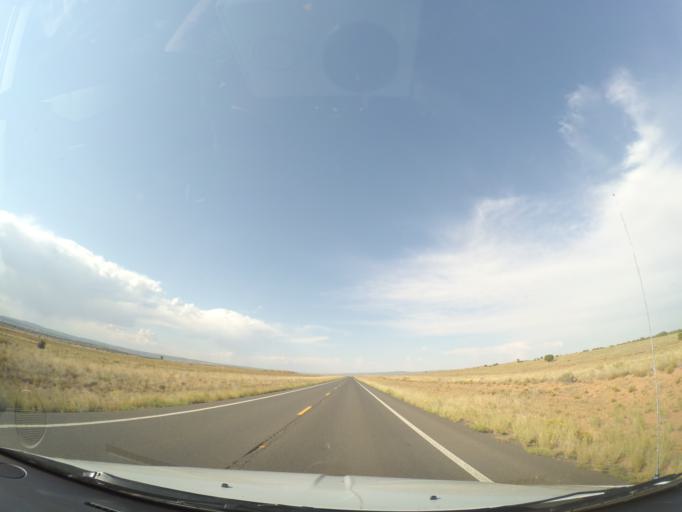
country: US
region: Arizona
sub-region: Coconino County
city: Tuba City
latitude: 36.3552
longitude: -111.4242
